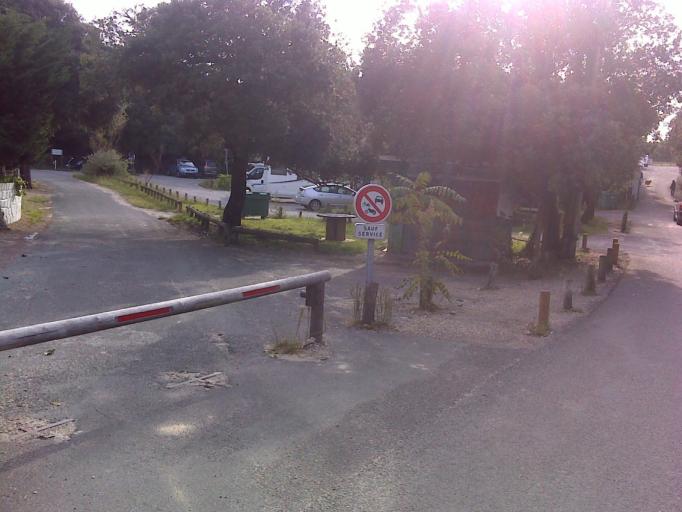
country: FR
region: Poitou-Charentes
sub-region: Departement de la Charente-Maritime
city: Les Mathes
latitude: 45.6969
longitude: -1.2307
